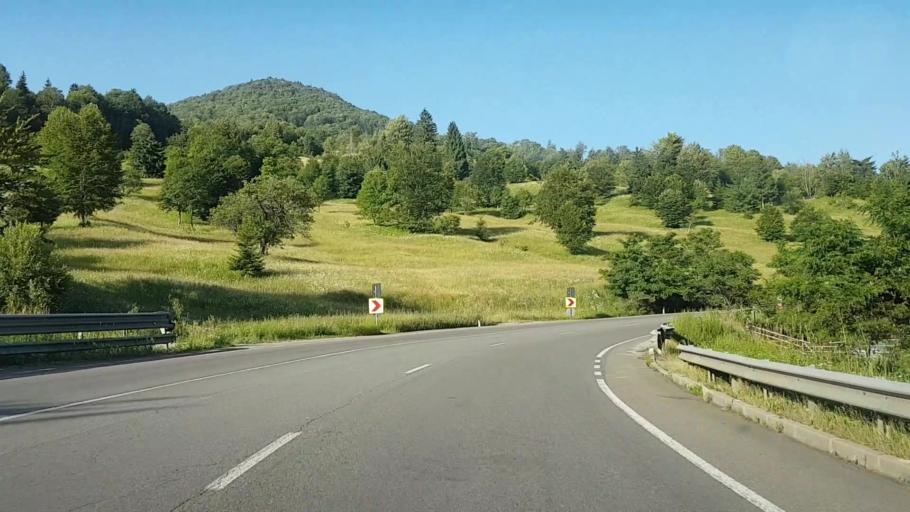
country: RO
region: Bistrita-Nasaud
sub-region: Comuna Tiha Bargaului
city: Tureac
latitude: 47.2238
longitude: 24.9266
